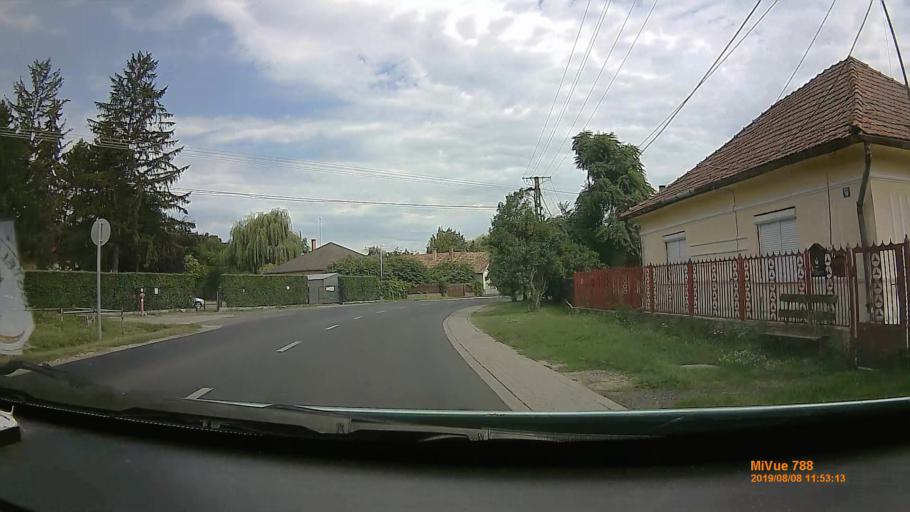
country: HU
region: Szabolcs-Szatmar-Bereg
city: Nyirmihalydi
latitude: 47.7313
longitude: 21.9597
